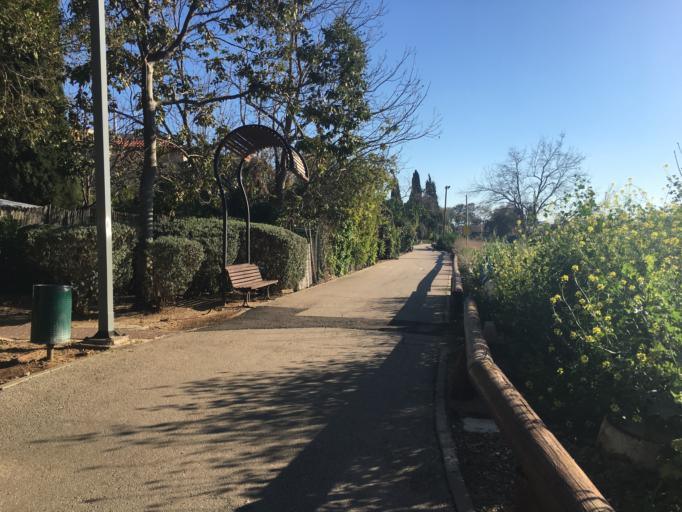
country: IL
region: Tel Aviv
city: Ramat HaSharon
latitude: 32.1435
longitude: 34.8262
